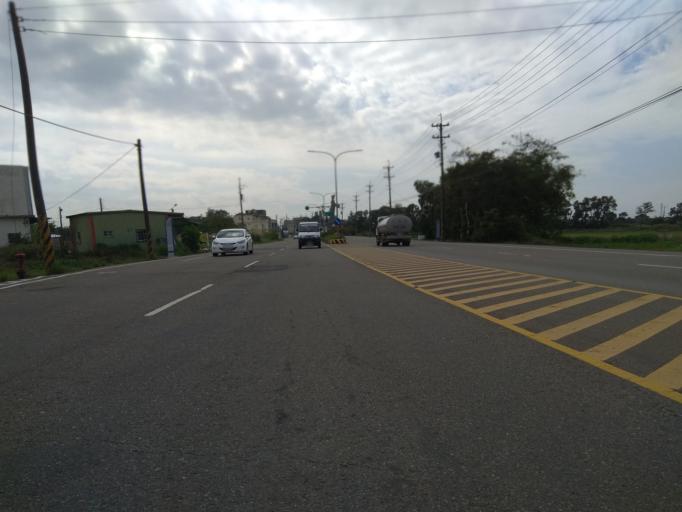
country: TW
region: Taiwan
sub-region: Hsinchu
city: Zhubei
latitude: 24.9797
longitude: 121.0269
